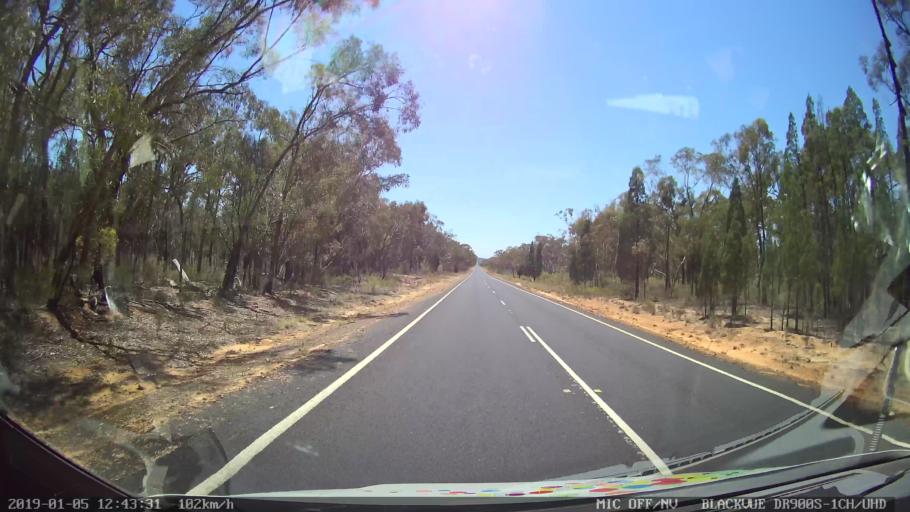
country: AU
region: New South Wales
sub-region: Warrumbungle Shire
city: Coonabarabran
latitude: -31.1472
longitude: 149.5252
